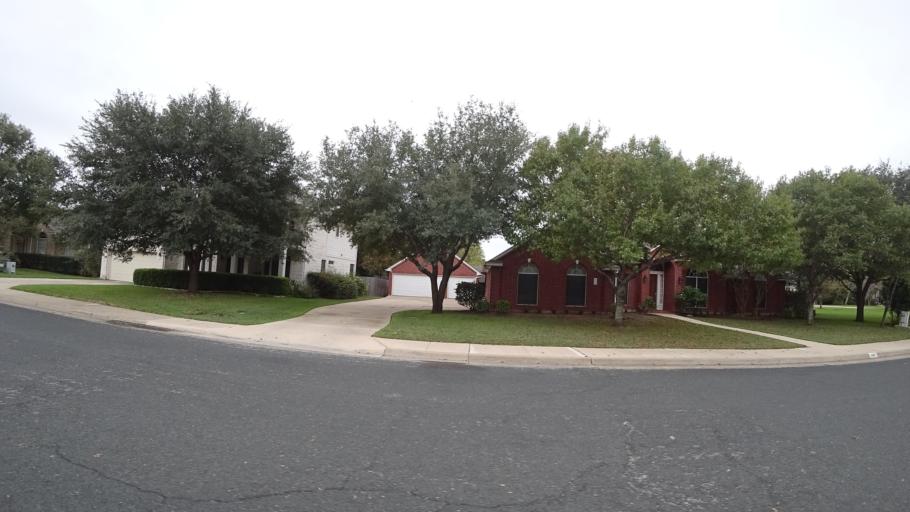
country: US
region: Texas
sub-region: Travis County
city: Shady Hollow
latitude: 30.1567
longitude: -97.8557
